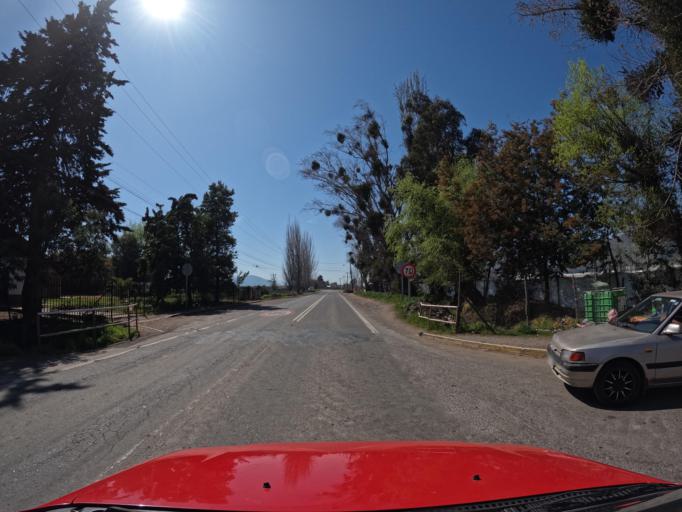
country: CL
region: Maule
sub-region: Provincia de Curico
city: Rauco
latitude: -35.0221
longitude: -71.4305
